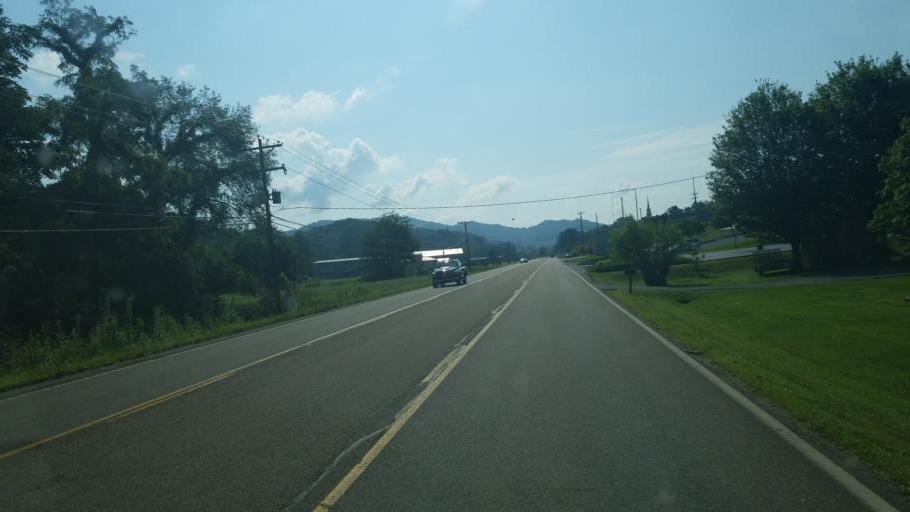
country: US
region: Tennessee
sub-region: Carter County
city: Roan Mountain
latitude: 36.1946
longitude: -82.0609
